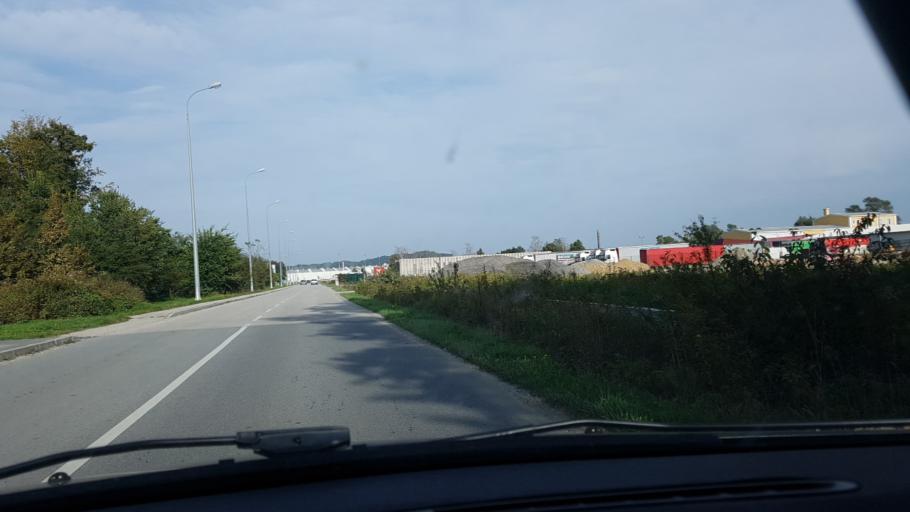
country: HR
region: Krapinsko-Zagorska
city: Zabok
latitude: 46.0162
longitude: 15.8875
